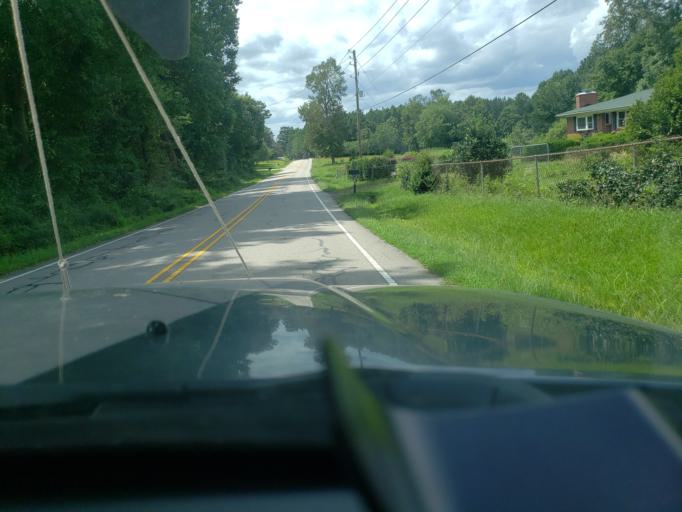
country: US
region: North Carolina
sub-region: Wake County
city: Rolesville
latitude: 35.8779
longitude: -78.4547
